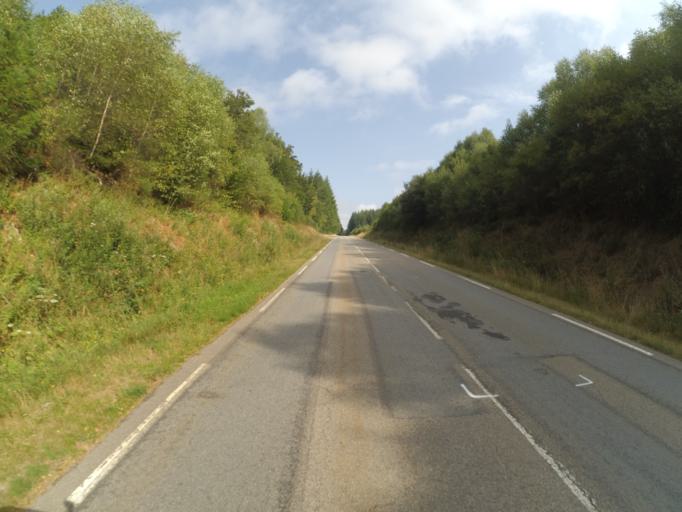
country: FR
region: Limousin
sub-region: Departement de la Correze
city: Meymac
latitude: 45.5885
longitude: 2.1302
